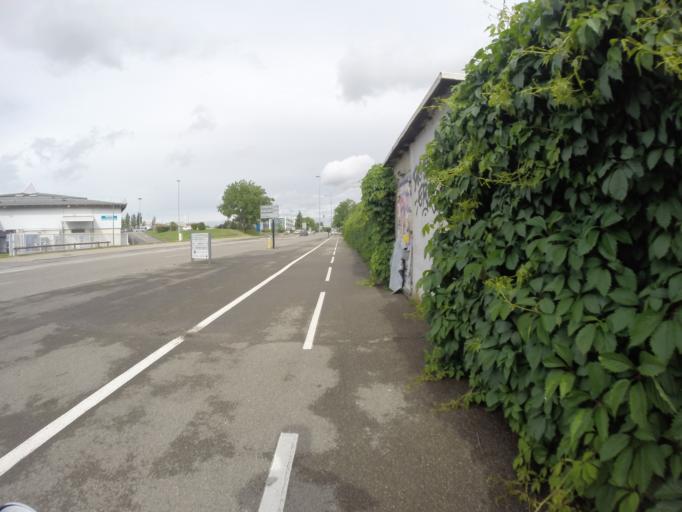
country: FR
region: Rhone-Alpes
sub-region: Departement du Rhone
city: Bron
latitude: 45.7267
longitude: 4.9297
